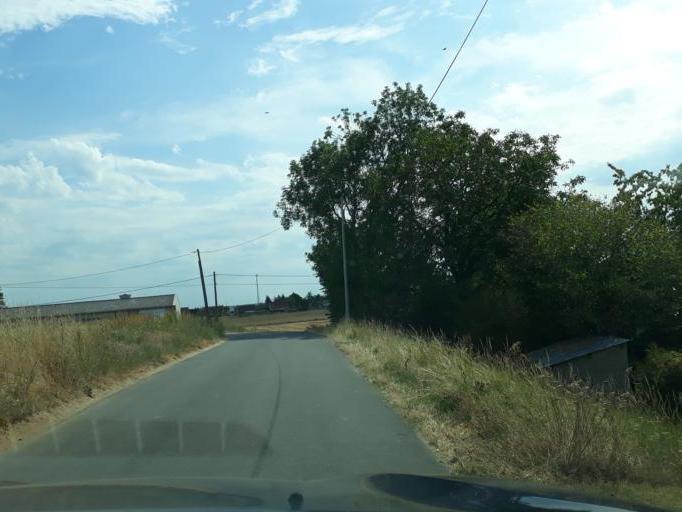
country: FR
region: Centre
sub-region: Departement du Loiret
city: Chateauneuf-sur-Loire
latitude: 47.8452
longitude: 2.2078
